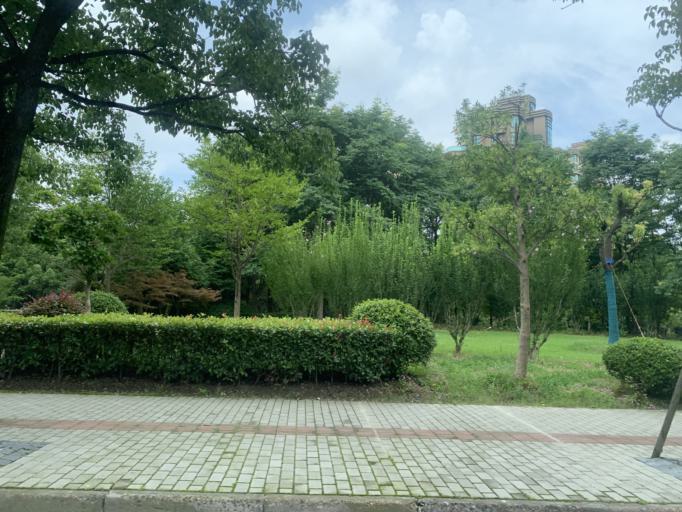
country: CN
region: Shanghai Shi
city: Huamu
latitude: 31.2056
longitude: 121.5313
